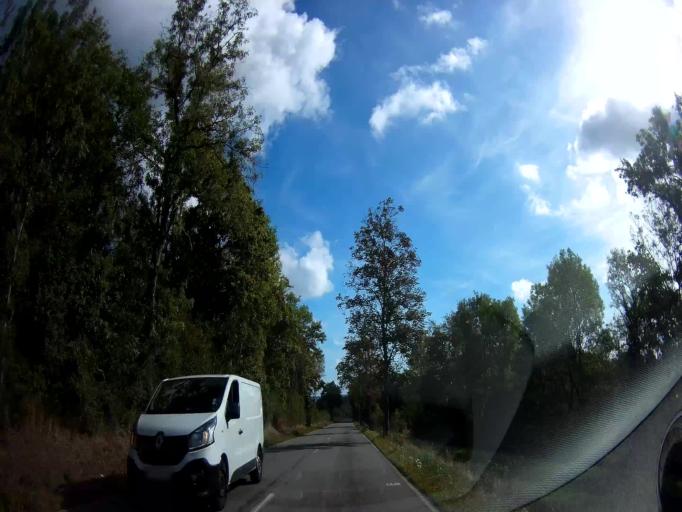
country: BE
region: Wallonia
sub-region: Province du Luxembourg
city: Wellin
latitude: 50.1722
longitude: 5.1195
